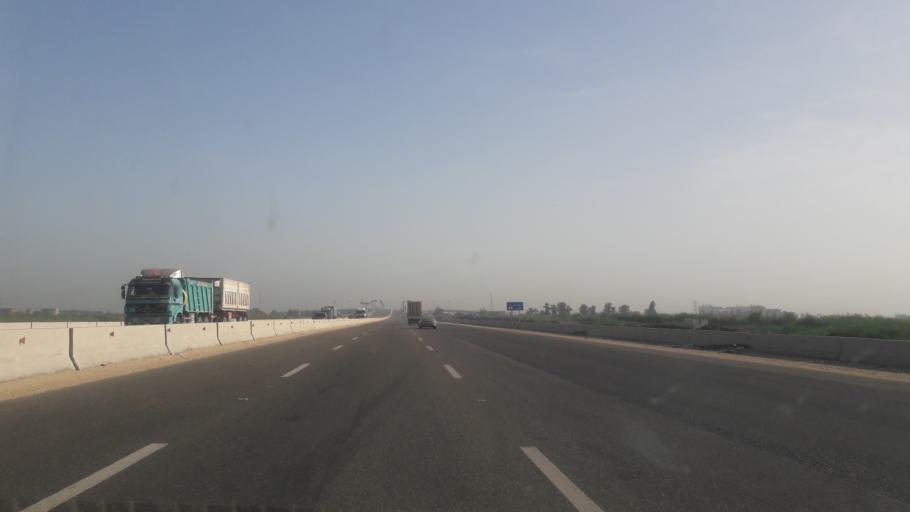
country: EG
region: Muhafazat Bur Sa`id
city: Port Said
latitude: 31.0081
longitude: 32.2368
